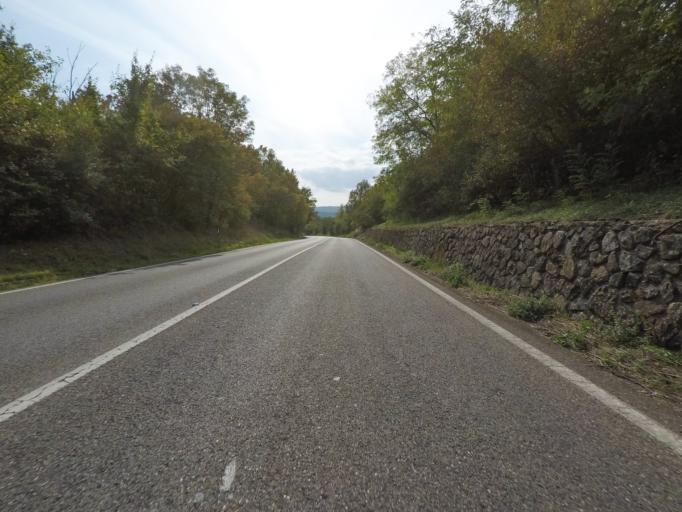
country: IT
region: Tuscany
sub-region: Provincia di Siena
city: Rosia
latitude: 43.1807
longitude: 11.2769
